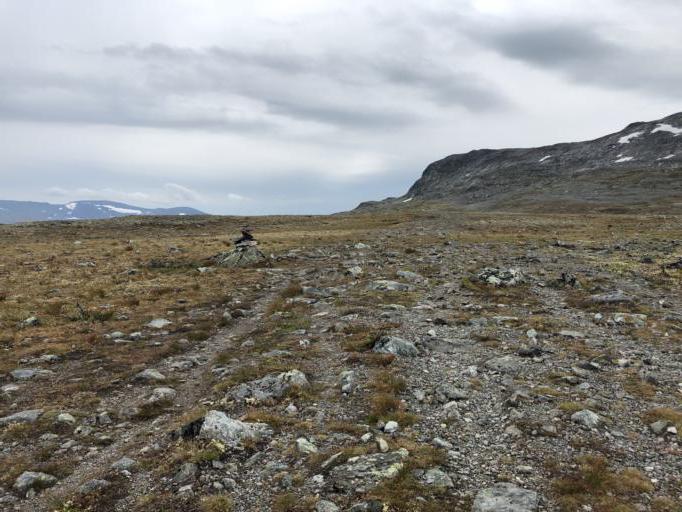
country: NO
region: Oppland
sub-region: Lom
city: Fossbergom
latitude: 61.5241
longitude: 8.8103
